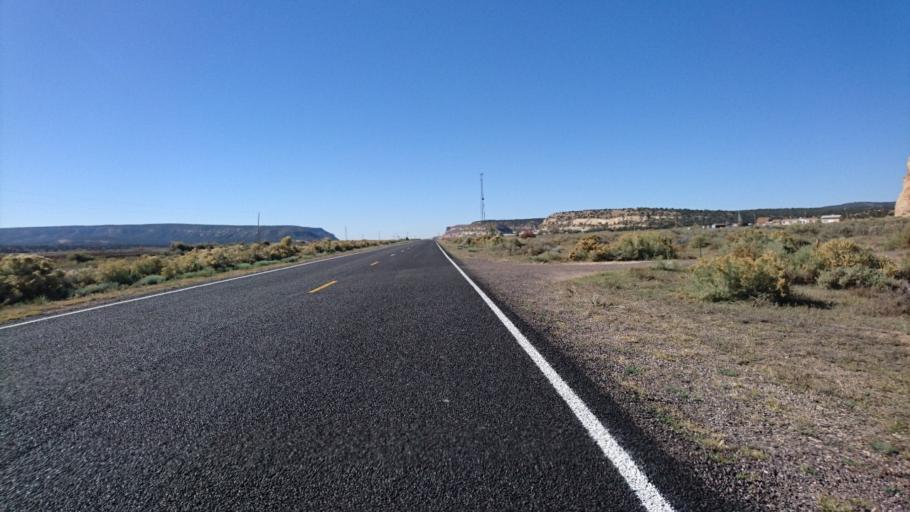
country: US
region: Arizona
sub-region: Apache County
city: Houck
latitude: 35.3990
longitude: -109.0156
